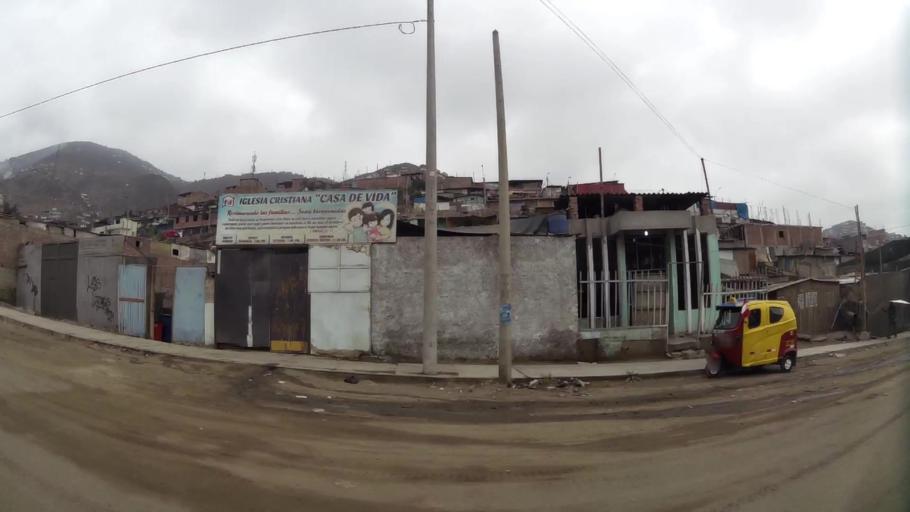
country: PE
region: Lima
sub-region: Lima
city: La Molina
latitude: -12.1272
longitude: -76.9519
